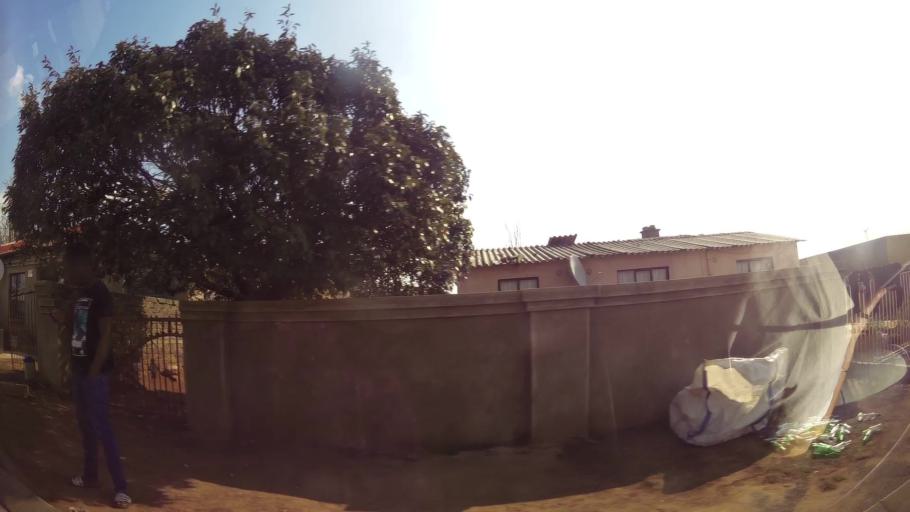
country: ZA
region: Gauteng
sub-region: Ekurhuleni Metropolitan Municipality
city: Germiston
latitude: -26.3114
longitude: 28.1548
